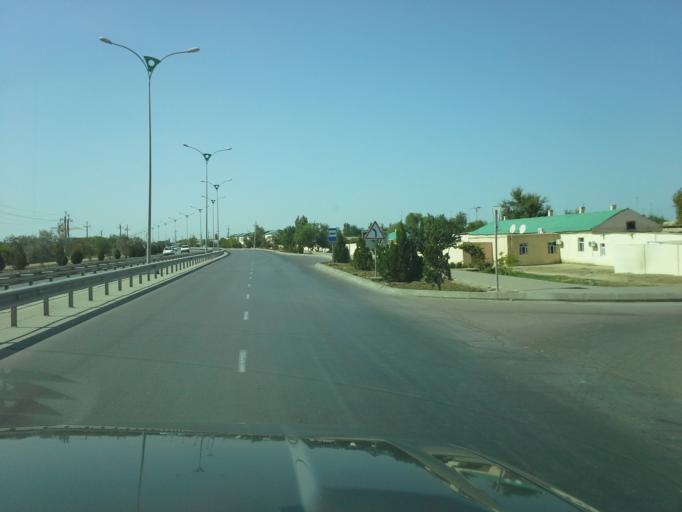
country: TM
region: Dasoguz
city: Dasoguz
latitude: 41.8495
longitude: 59.9284
